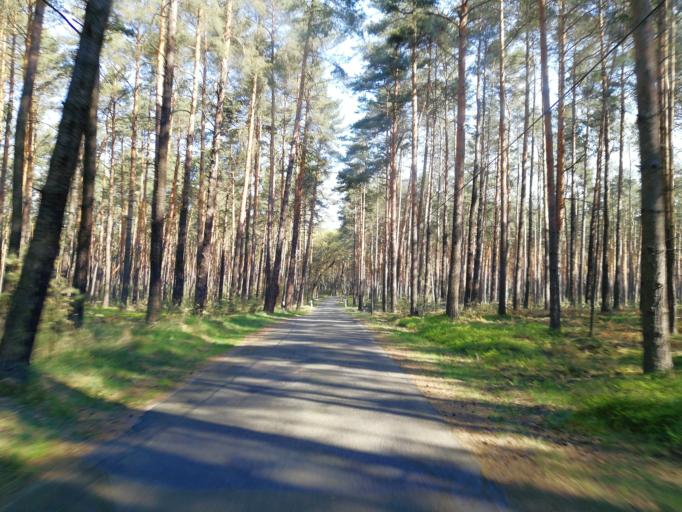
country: DE
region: Brandenburg
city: Bronkow
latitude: 51.6830
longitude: 13.8645
